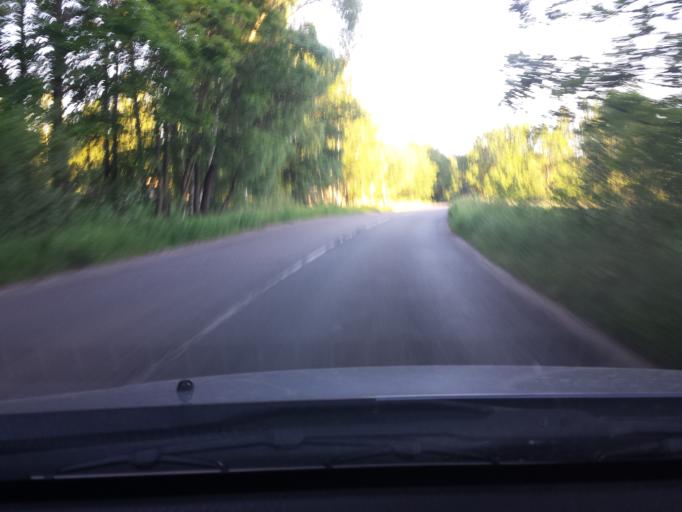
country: LV
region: Riga
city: Jaunciems
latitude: 57.0165
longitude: 24.2113
